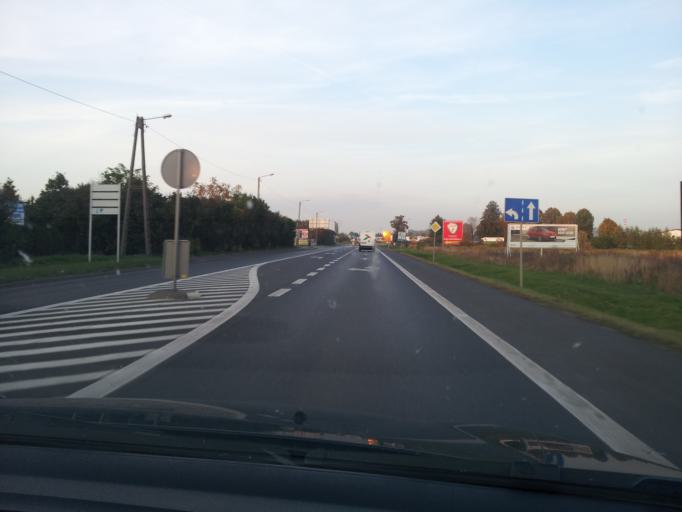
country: PL
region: Kujawsko-Pomorskie
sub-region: Powiat inowroclawski
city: Inowroclaw
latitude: 52.8064
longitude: 18.2739
